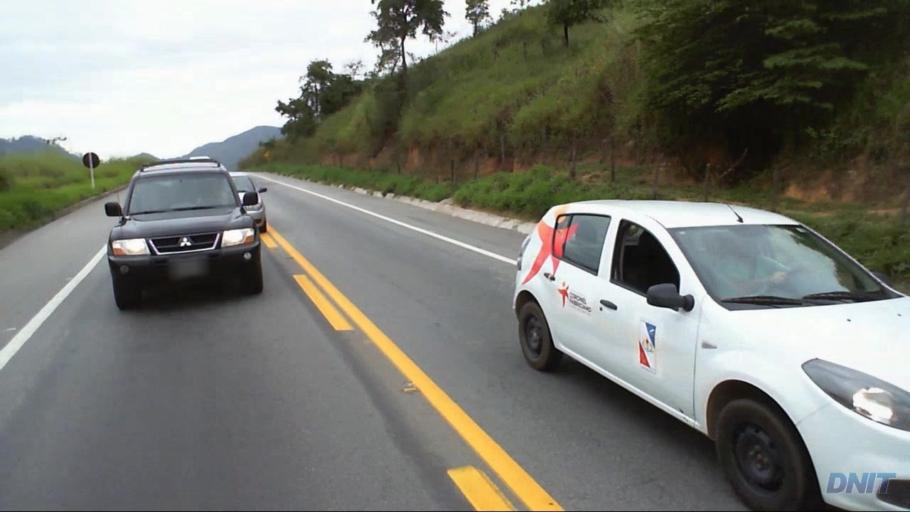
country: BR
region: Minas Gerais
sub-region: Timoteo
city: Timoteo
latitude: -19.6009
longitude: -42.7539
